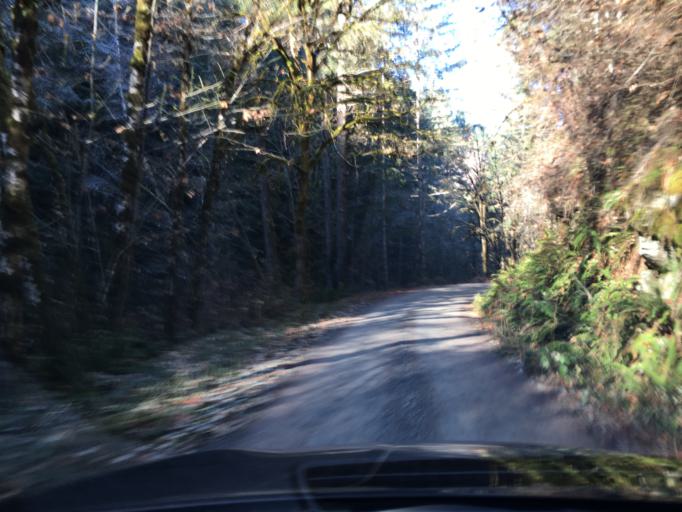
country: US
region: Oregon
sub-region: Douglas County
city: Winston
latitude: 43.3219
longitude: -123.5801
